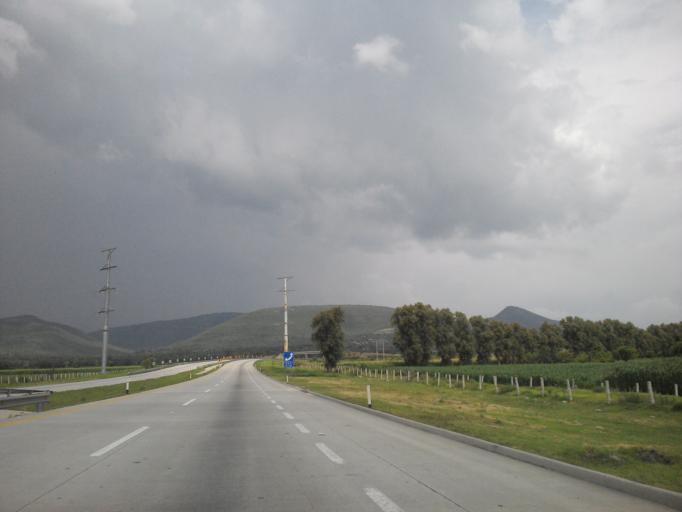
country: MX
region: Hidalgo
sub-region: Atitalaquia
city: Tezoquipa
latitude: 20.0618
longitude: -99.2017
